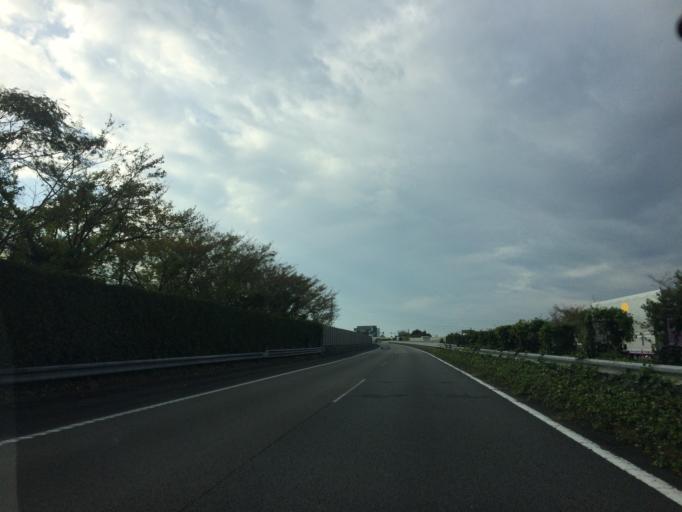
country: JP
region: Shizuoka
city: Shizuoka-shi
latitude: 35.0087
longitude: 138.4341
